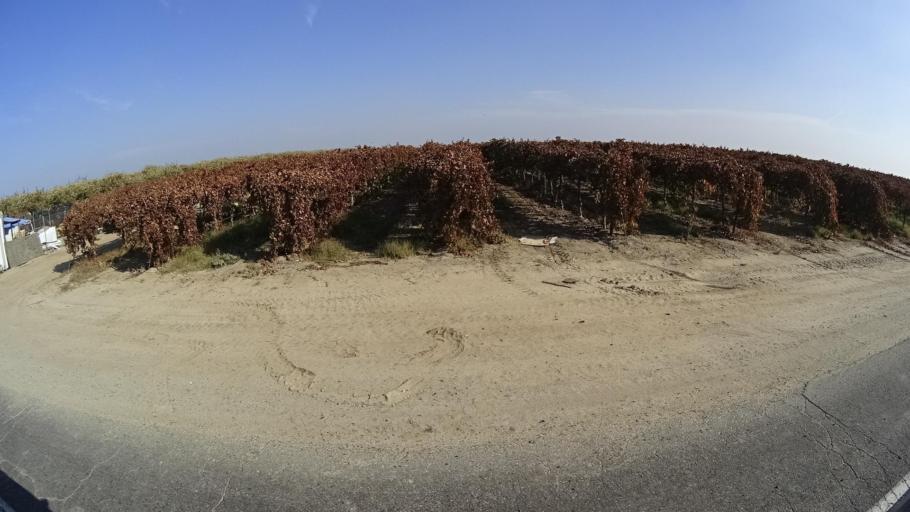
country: US
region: California
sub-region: Kern County
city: McFarland
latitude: 35.6524
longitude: -119.1957
